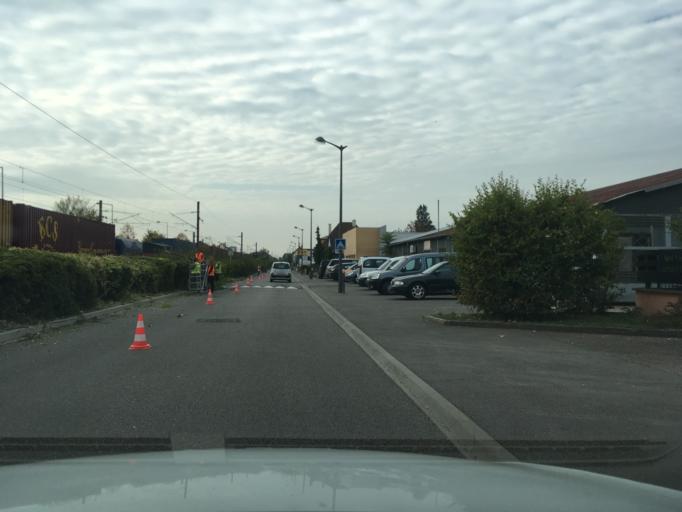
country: FR
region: Alsace
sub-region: Departement du Haut-Rhin
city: Colmar
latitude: 48.0905
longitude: 7.3508
